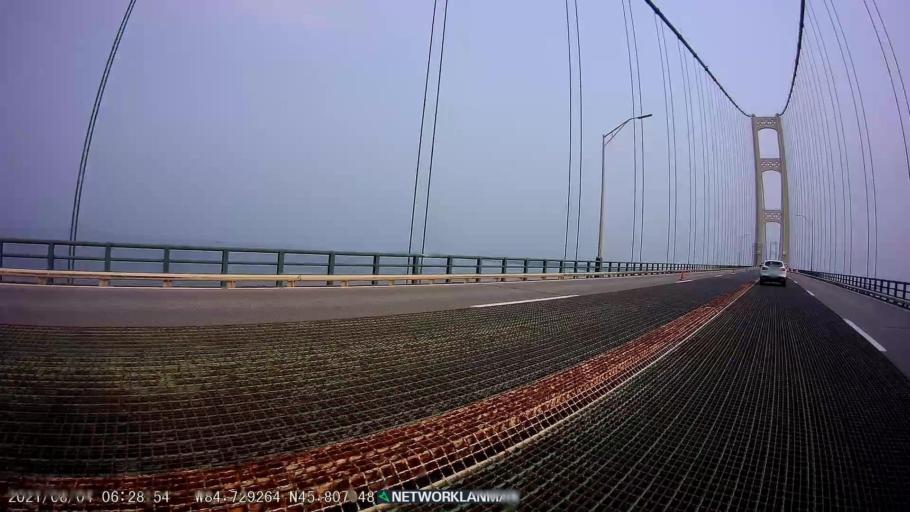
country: US
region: Michigan
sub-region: Mackinac County
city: Saint Ignace
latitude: 45.8075
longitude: -84.7286
